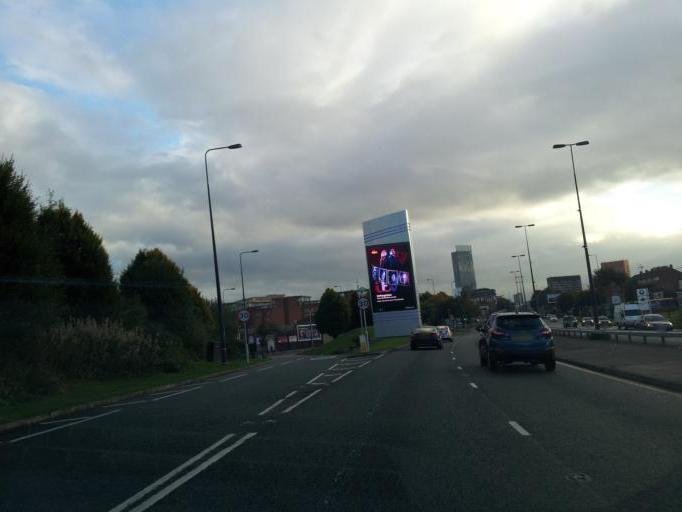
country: GB
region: England
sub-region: Manchester
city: Hulme
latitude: 53.4687
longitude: -2.2683
